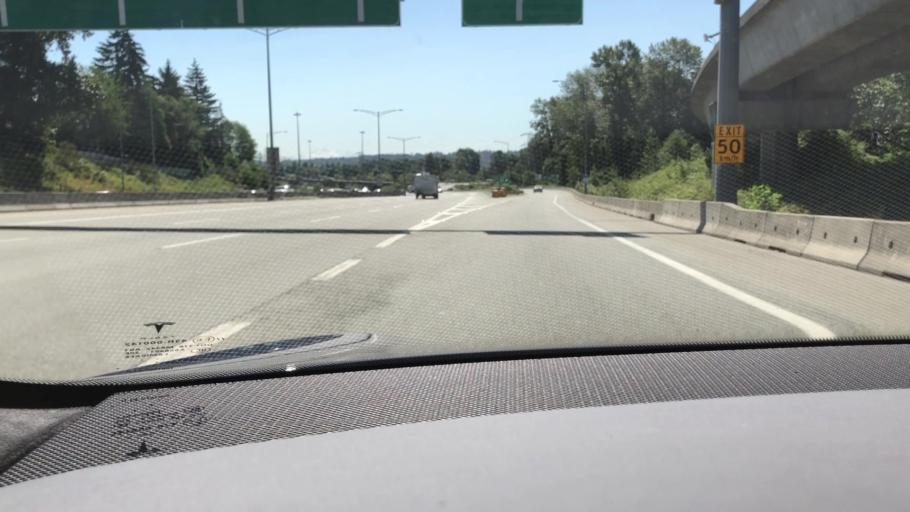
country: CA
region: British Columbia
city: New Westminster
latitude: 49.2371
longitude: -122.8846
